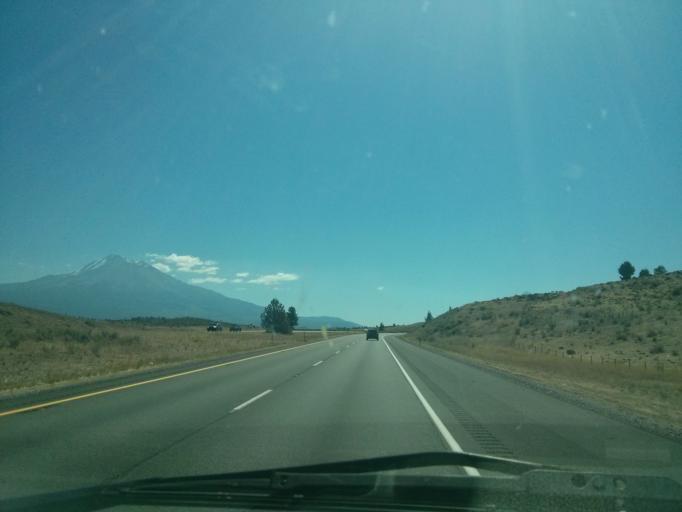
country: US
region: California
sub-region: Siskiyou County
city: Weed
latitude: 41.5005
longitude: -122.4676
